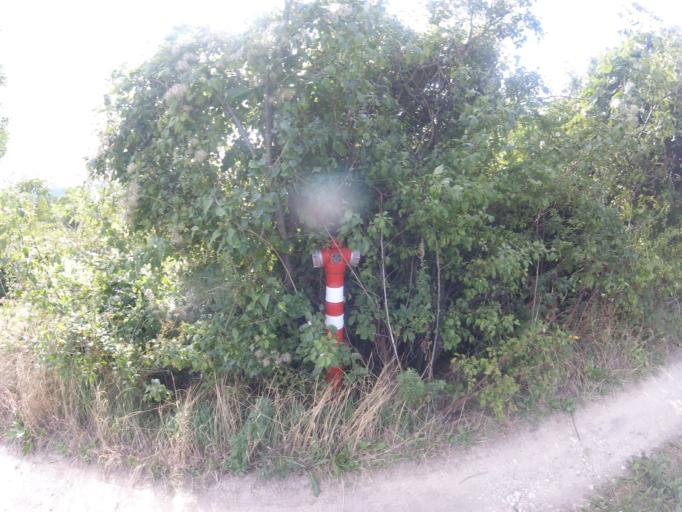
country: HU
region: Pest
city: Zsambek
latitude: 47.5749
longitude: 18.7301
